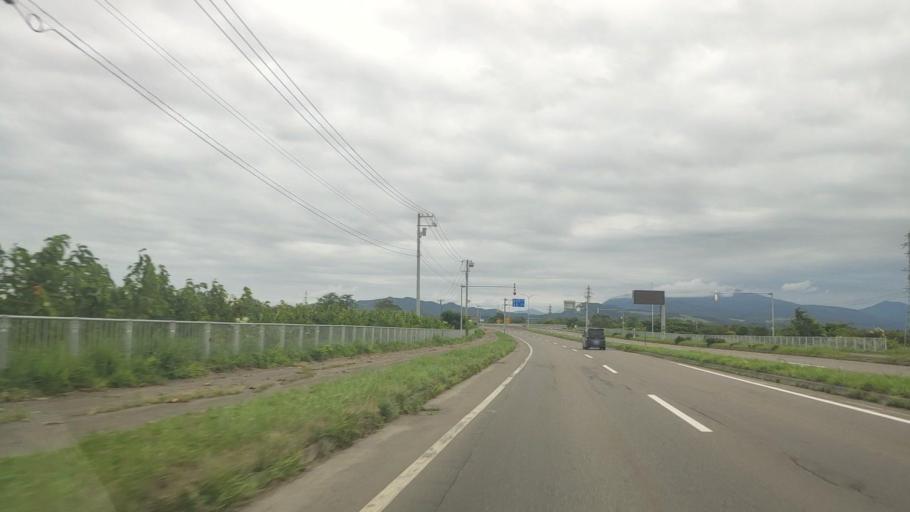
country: JP
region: Hokkaido
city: Nanae
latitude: 42.2667
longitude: 140.2727
